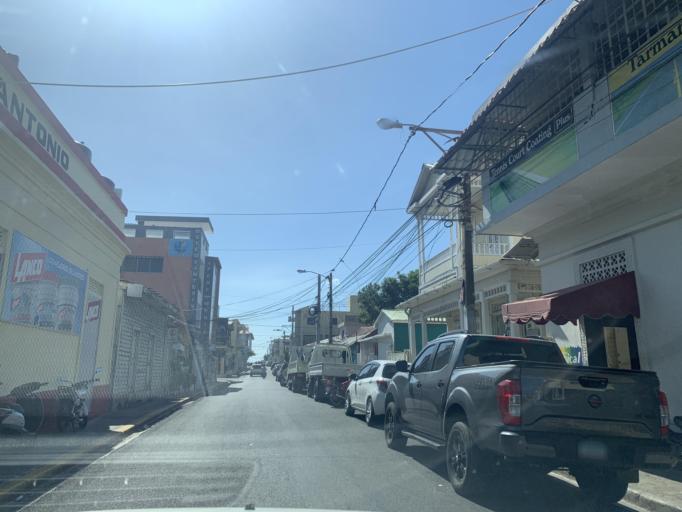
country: DO
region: Puerto Plata
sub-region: Puerto Plata
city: Puerto Plata
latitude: 19.7962
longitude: -70.6877
